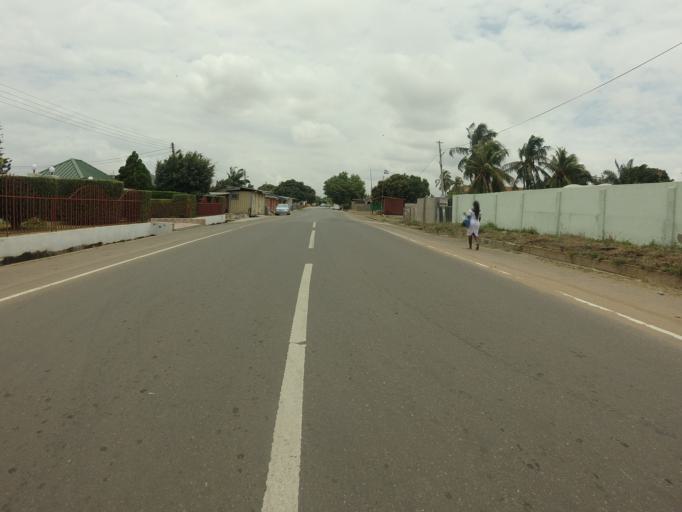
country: GH
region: Greater Accra
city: Nungua
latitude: 5.6116
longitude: -0.0769
